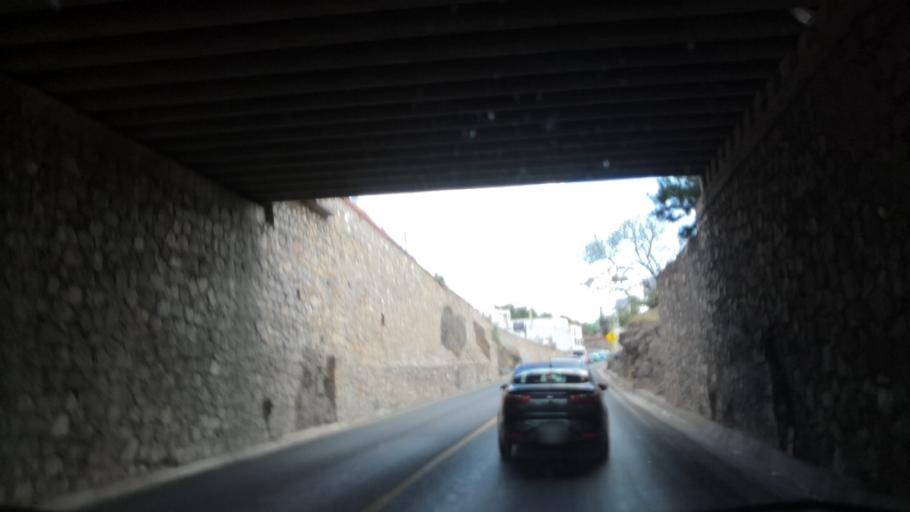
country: MX
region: Guanajuato
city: Marfil
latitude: 20.9970
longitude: -101.2853
